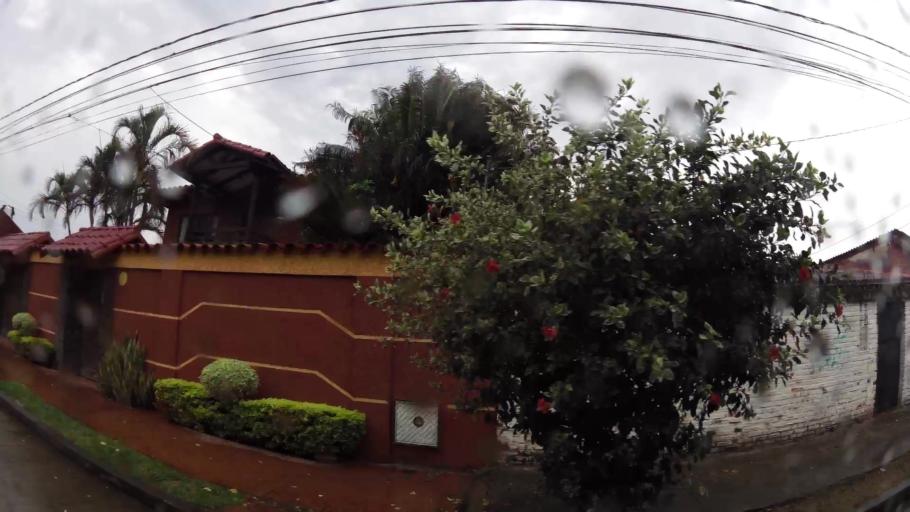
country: BO
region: Santa Cruz
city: Santa Cruz de la Sierra
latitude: -17.8044
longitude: -63.1557
